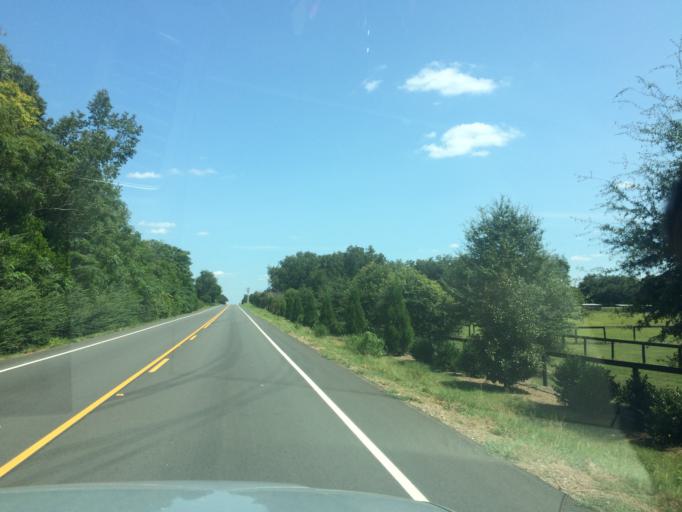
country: US
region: South Carolina
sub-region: Aiken County
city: Aiken
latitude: 33.5725
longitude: -81.5514
